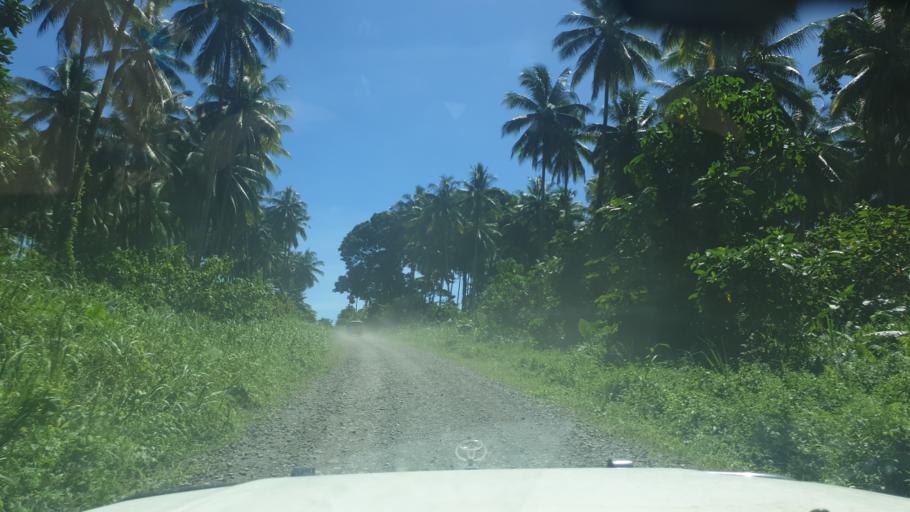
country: PG
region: Bougainville
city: Buka
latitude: -5.6668
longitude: 155.1006
